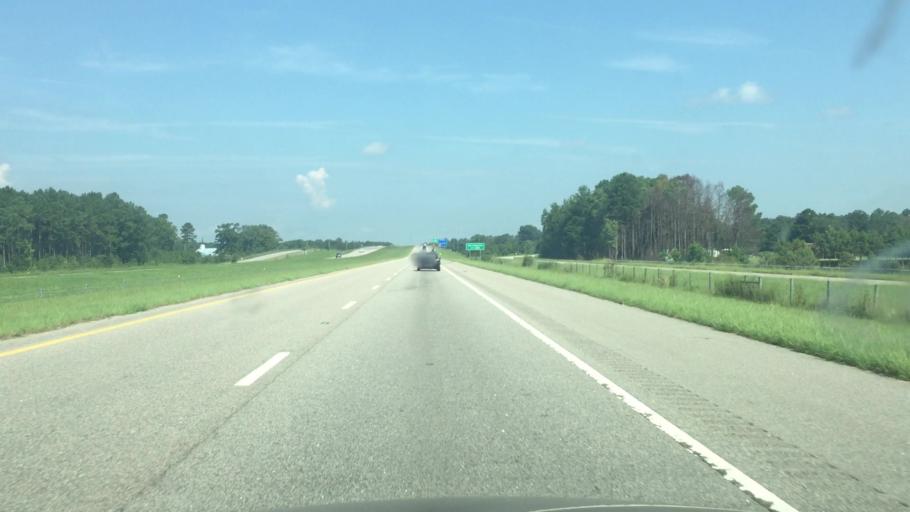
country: US
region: North Carolina
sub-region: Robeson County
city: Pembroke
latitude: 34.6448
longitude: -79.2387
